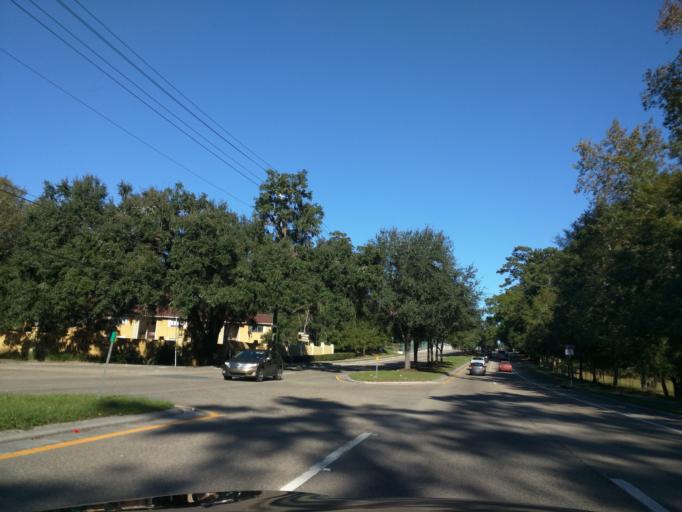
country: US
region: Florida
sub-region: Leon County
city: Tallahassee
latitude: 30.4653
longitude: -84.2380
